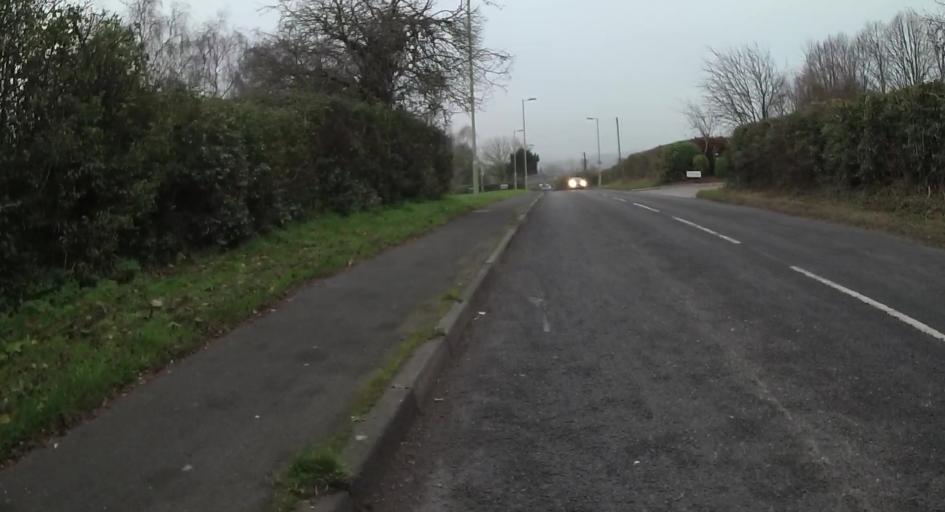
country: GB
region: England
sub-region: Hampshire
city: Kings Worthy
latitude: 51.0991
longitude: -1.2960
